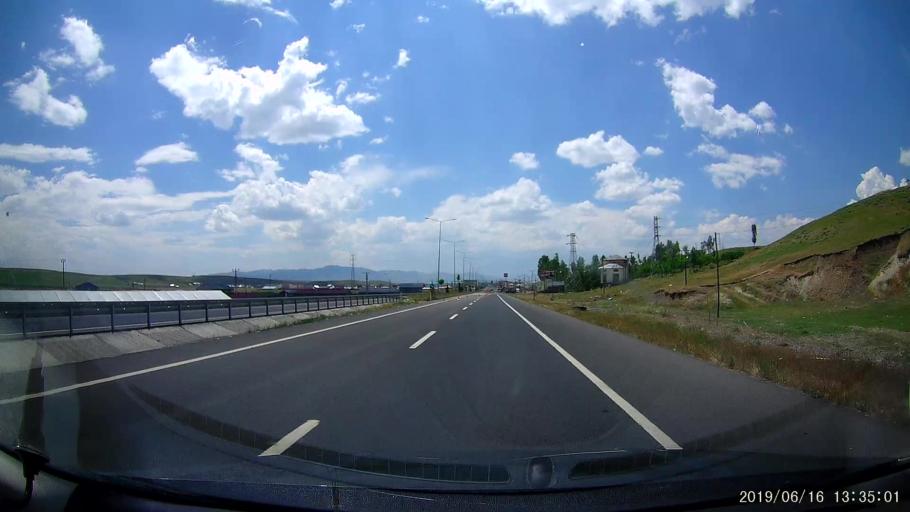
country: TR
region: Agri
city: Agri
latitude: 39.7129
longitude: 43.1138
